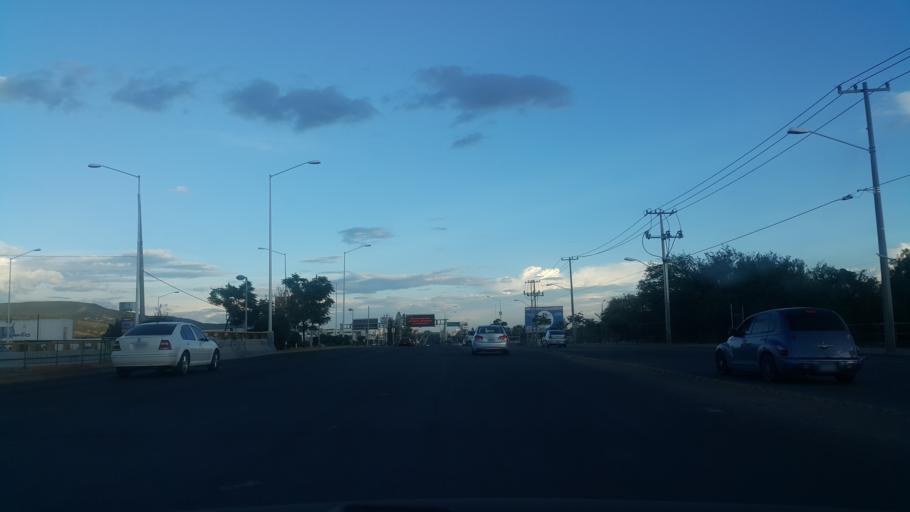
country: MX
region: Guanajuato
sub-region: Leon
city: Medina
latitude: 21.1685
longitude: -101.6547
